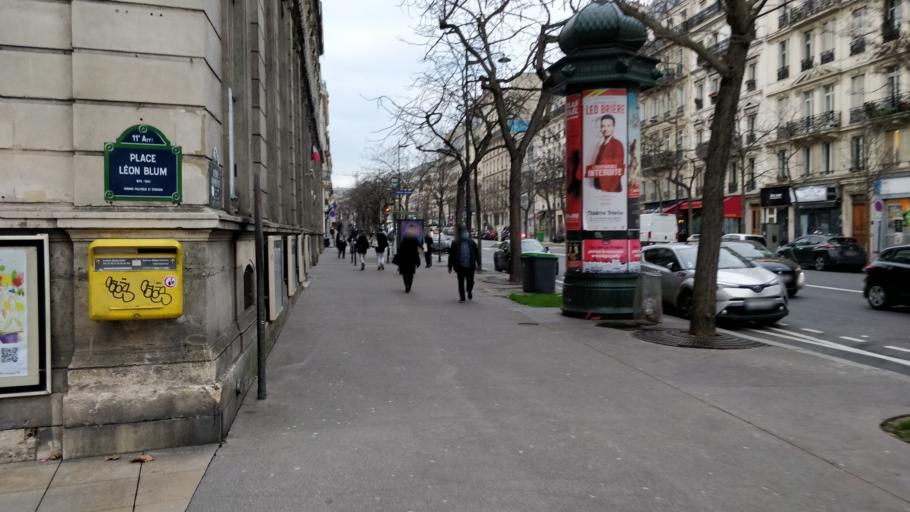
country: FR
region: Ile-de-France
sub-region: Paris
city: Paris
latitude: 48.8586
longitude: 2.3797
